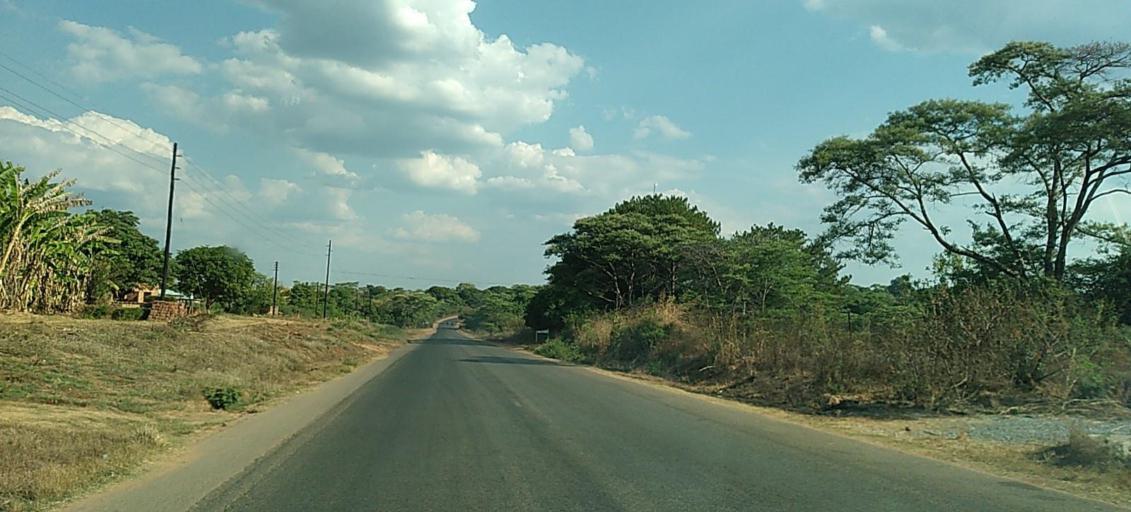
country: ZM
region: Copperbelt
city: Luanshya
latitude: -13.3444
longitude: 28.4188
